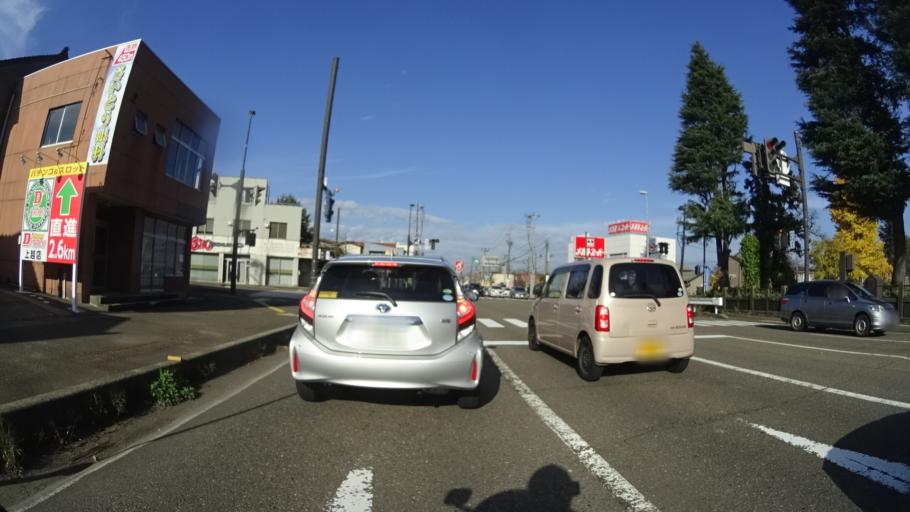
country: JP
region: Niigata
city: Joetsu
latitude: 37.1144
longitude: 138.2511
